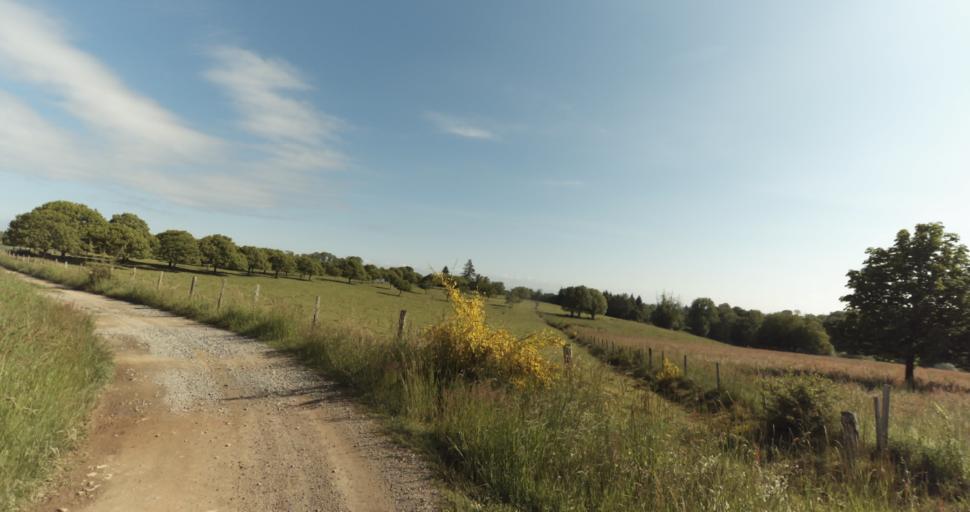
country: FR
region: Limousin
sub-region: Departement de la Haute-Vienne
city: Solignac
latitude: 45.7219
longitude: 1.2437
